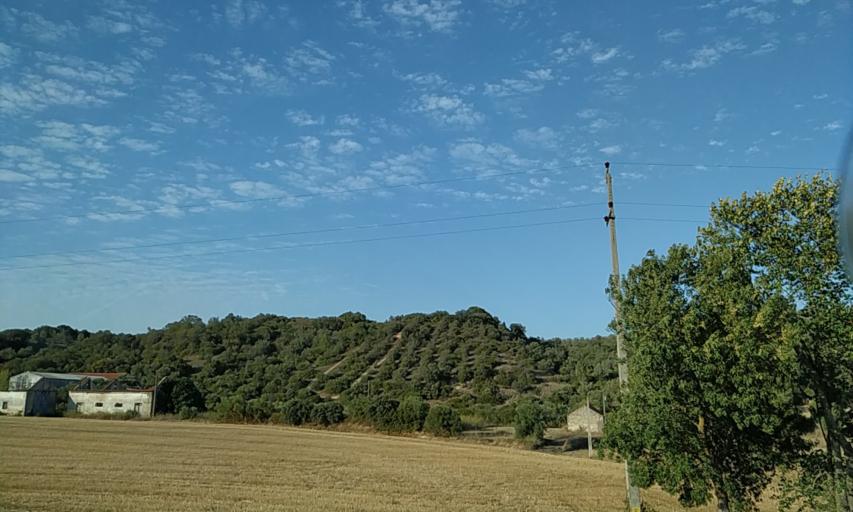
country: PT
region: Santarem
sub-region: Alcanena
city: Alcanena
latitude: 39.3653
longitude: -8.6548
